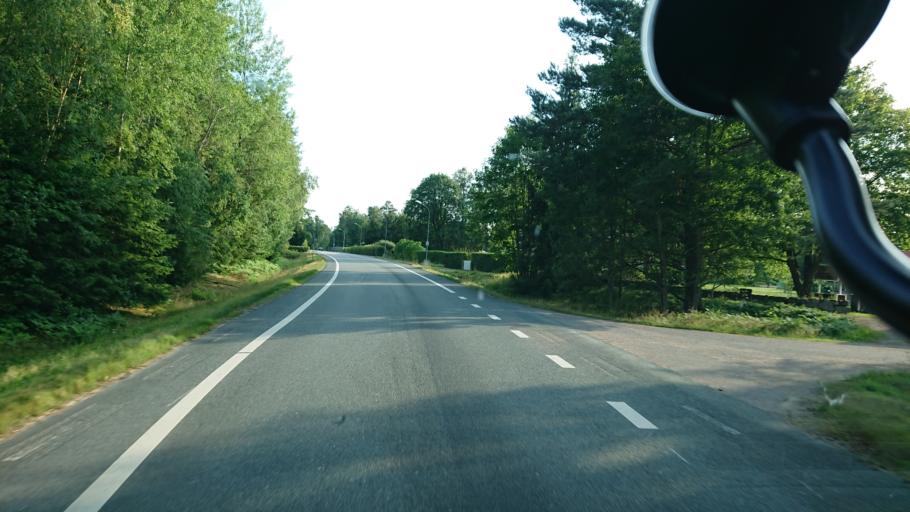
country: SE
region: Kronoberg
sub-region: Vaxjo Kommun
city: Rottne
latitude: 57.0325
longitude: 14.8975
